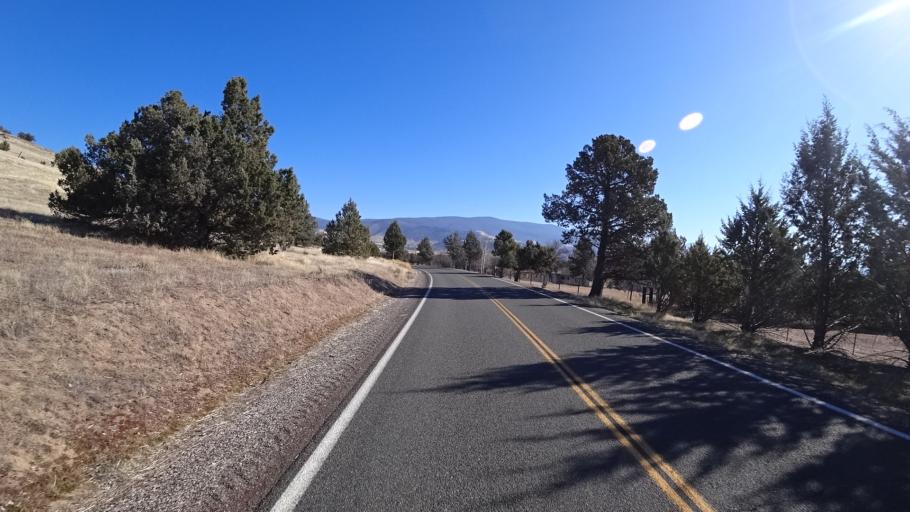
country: US
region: California
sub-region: Siskiyou County
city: Montague
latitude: 41.6590
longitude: -122.3728
